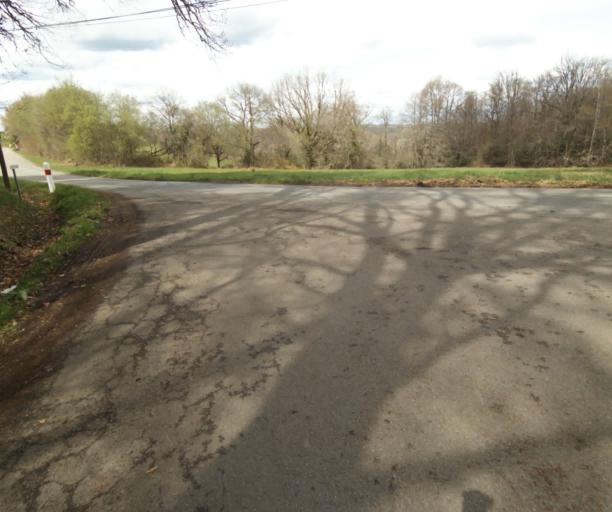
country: FR
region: Limousin
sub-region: Departement de la Correze
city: Laguenne
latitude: 45.2244
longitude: 1.8836
